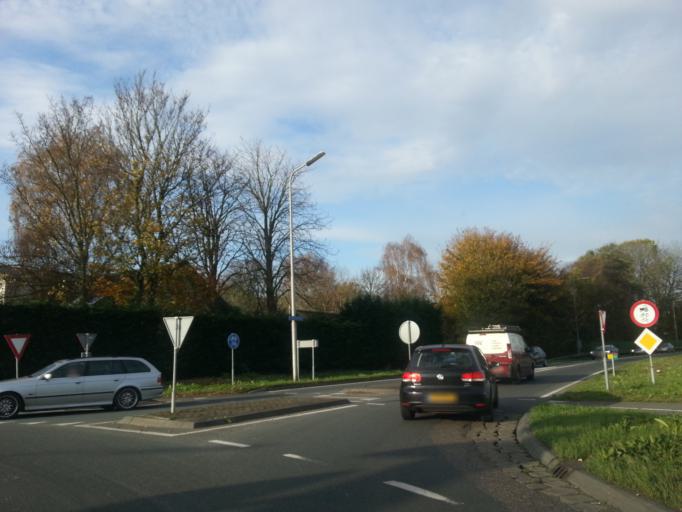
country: NL
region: South Holland
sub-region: Gemeente Capelle aan den IJssel
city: Capelle aan den IJssel
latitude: 51.9890
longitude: 4.6005
